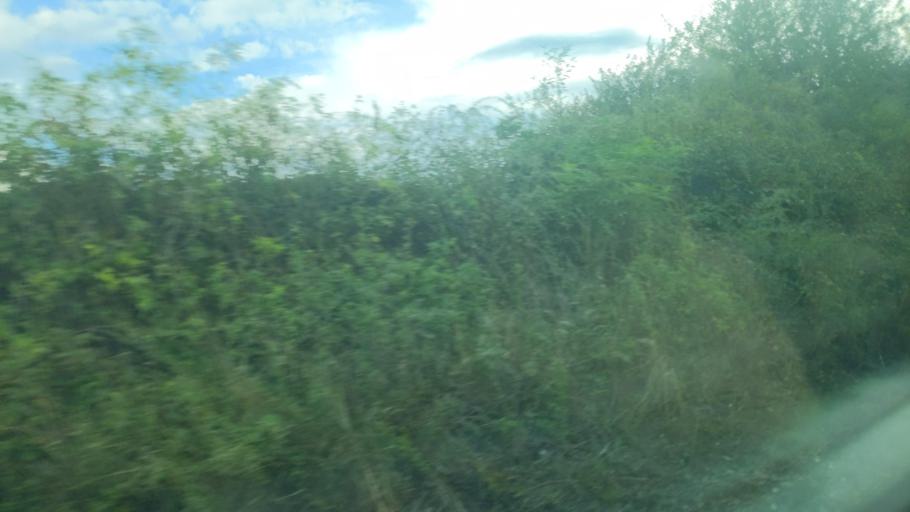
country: CZ
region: Central Bohemia
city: Cesky Brod
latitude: 50.0789
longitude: 14.8100
